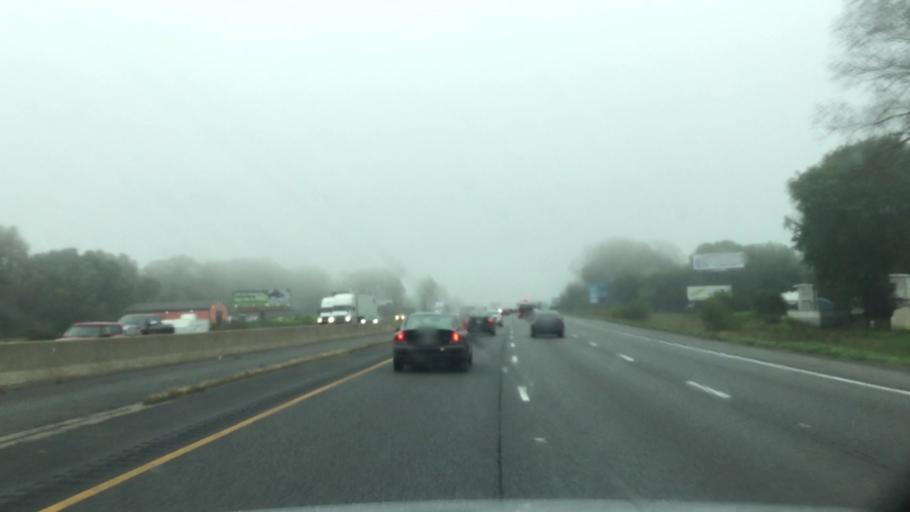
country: US
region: Indiana
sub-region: Porter County
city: Ogden Dunes
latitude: 41.5970
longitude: -87.2101
